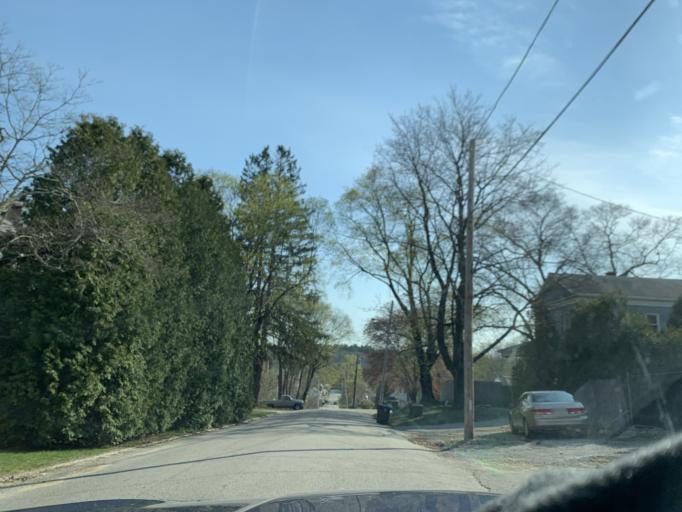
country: US
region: Rhode Island
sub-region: Kent County
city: West Warwick
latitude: 41.7289
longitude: -71.5343
